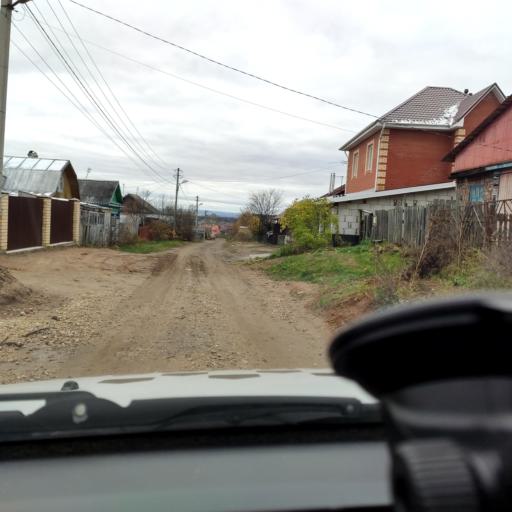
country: RU
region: Perm
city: Kondratovo
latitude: 58.0476
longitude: 56.1178
